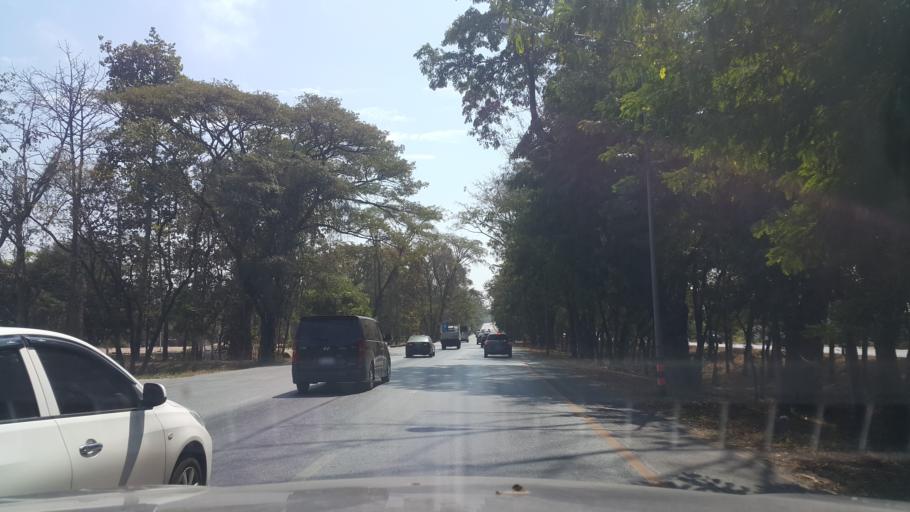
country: TH
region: Nakhon Ratchasima
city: Nakhon Ratchasima
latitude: 14.9208
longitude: 102.0629
